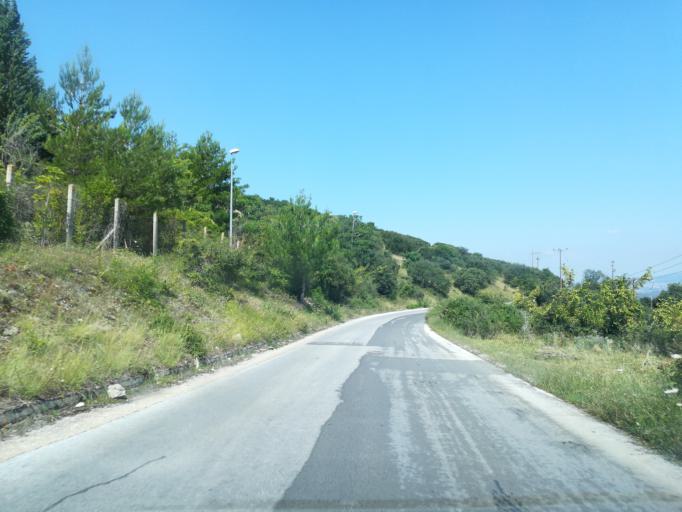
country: GR
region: Central Macedonia
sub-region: Nomos Thessalonikis
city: Asvestochori
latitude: 40.6348
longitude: 23.0216
